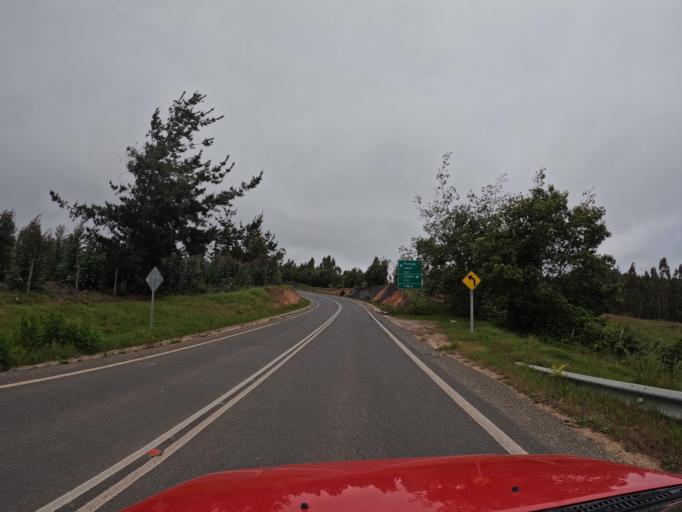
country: CL
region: O'Higgins
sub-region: Provincia de Colchagua
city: Santa Cruz
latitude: -34.6155
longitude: -72.0123
